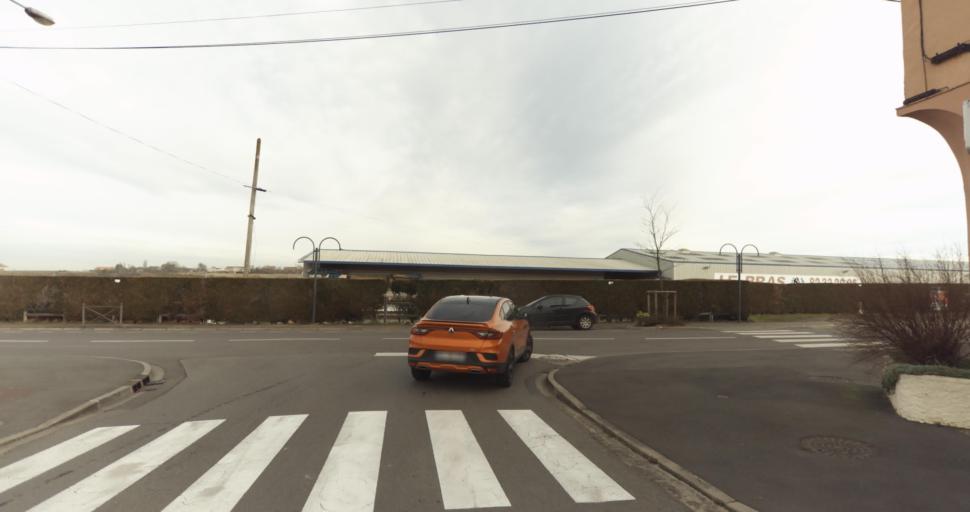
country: FR
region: Lorraine
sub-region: Departement de Meurthe-et-Moselle
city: Labry
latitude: 49.1647
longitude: 5.8762
